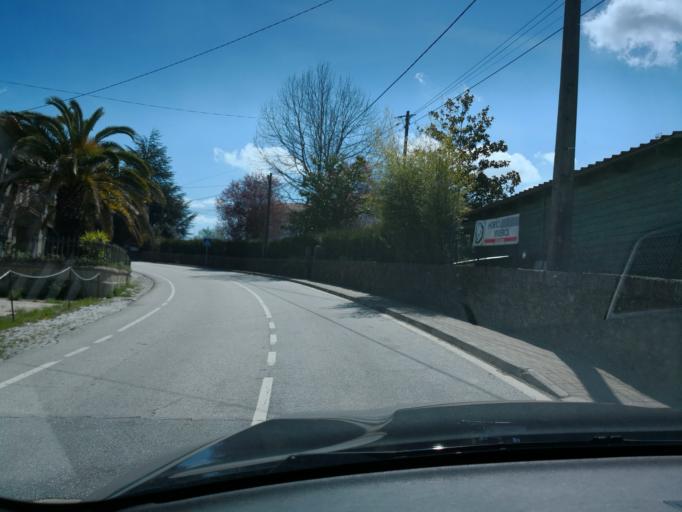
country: PT
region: Vila Real
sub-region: Vila Real
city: Vila Real
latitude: 41.2803
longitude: -7.6950
